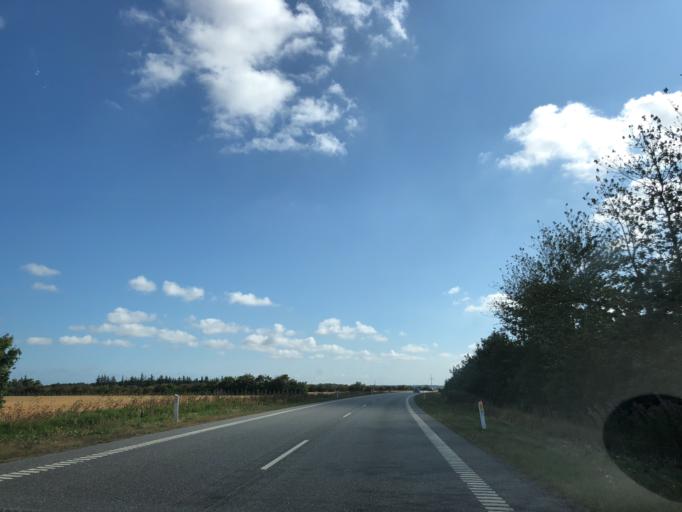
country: DK
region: North Denmark
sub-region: Jammerbugt Kommune
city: Fjerritslev
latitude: 57.0647
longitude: 9.1966
